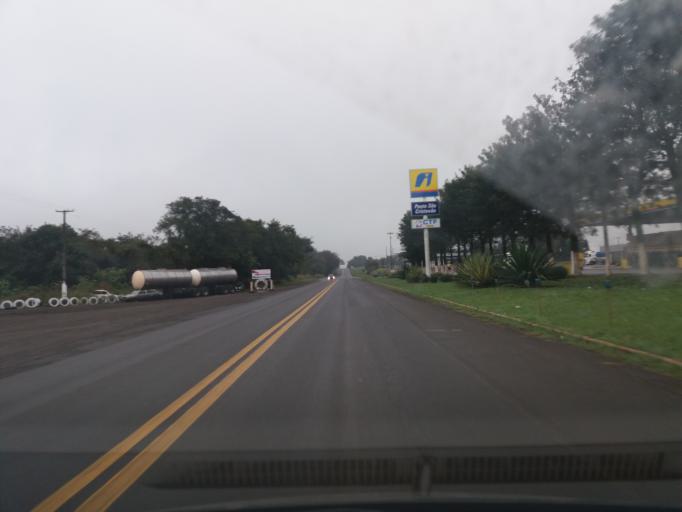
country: BR
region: Parana
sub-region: Ampere
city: Ampere
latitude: -25.8906
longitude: -53.4630
